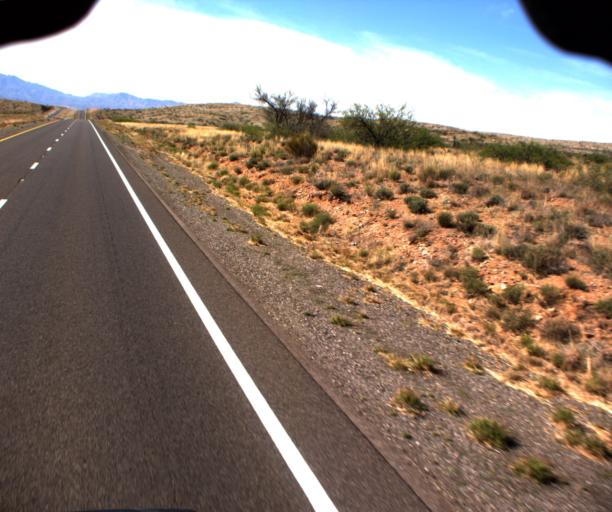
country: US
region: Arizona
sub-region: Cochise County
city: Willcox
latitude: 32.4373
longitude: -109.6639
